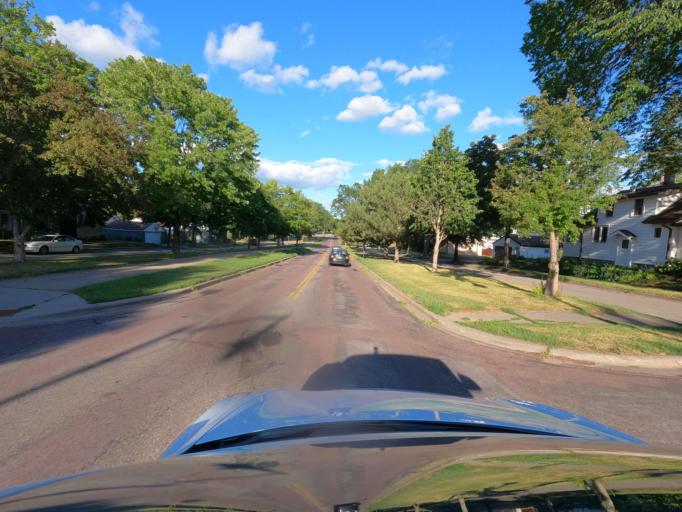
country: US
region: Minnesota
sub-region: Hennepin County
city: Saint Anthony
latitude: 45.0239
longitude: -93.2396
